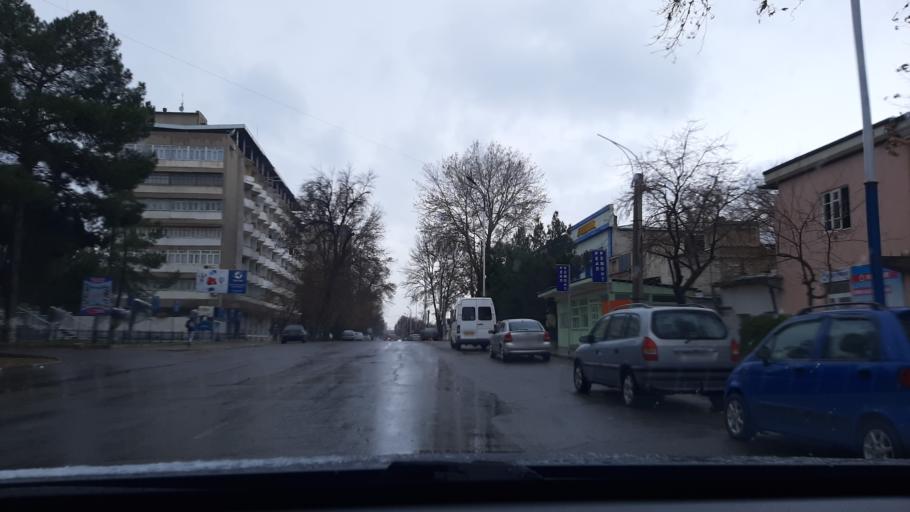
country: TJ
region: Viloyati Sughd
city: Khujand
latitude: 40.2782
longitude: 69.6402
